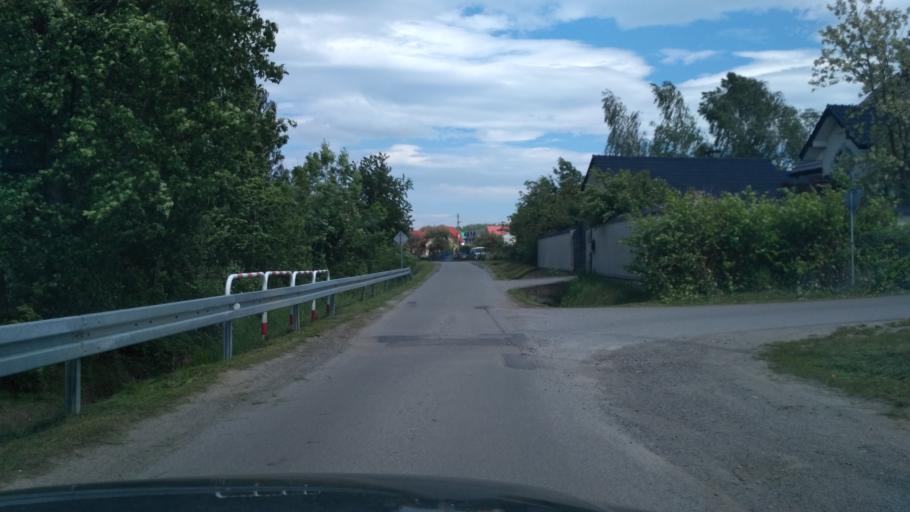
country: PL
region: Subcarpathian Voivodeship
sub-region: Powiat ropczycko-sedziszowski
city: Ropczyce
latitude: 50.0507
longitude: 21.6174
